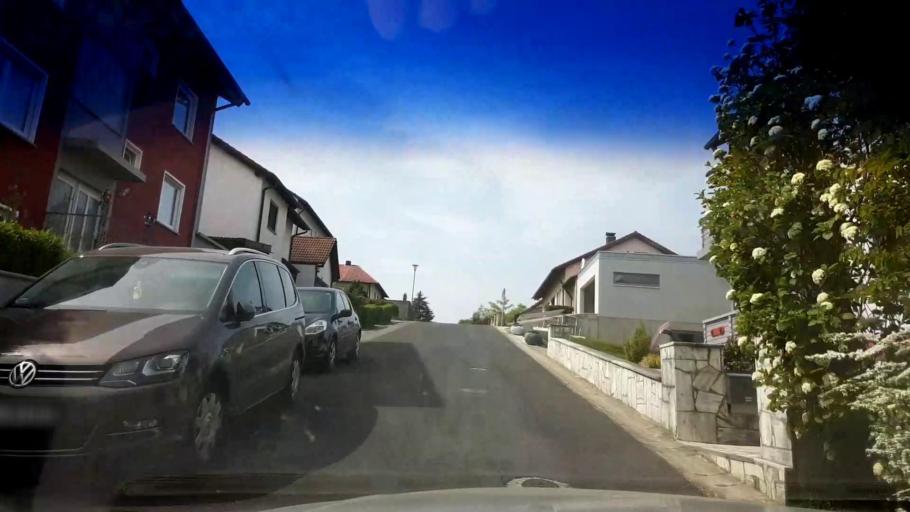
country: DE
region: Bavaria
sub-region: Upper Franconia
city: Baunach
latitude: 49.9875
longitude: 10.8453
